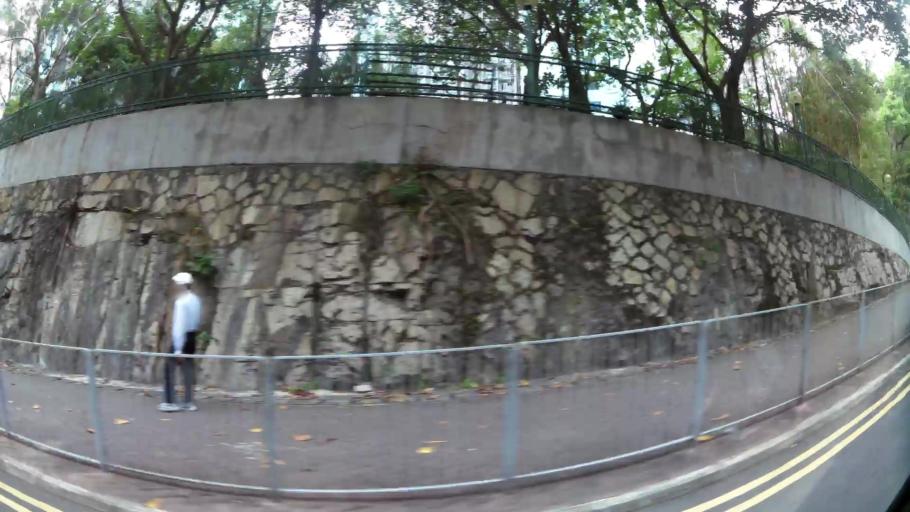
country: HK
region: Wanchai
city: Wan Chai
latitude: 22.2809
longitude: 114.2181
